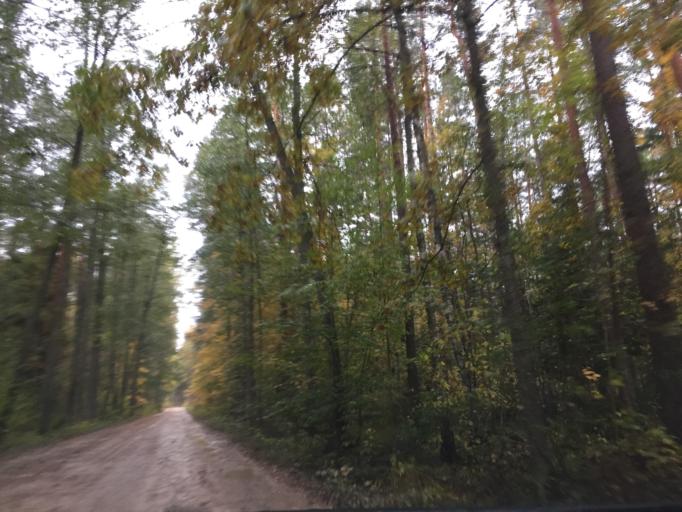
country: LV
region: Engure
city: Smarde
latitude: 56.9269
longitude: 23.4739
